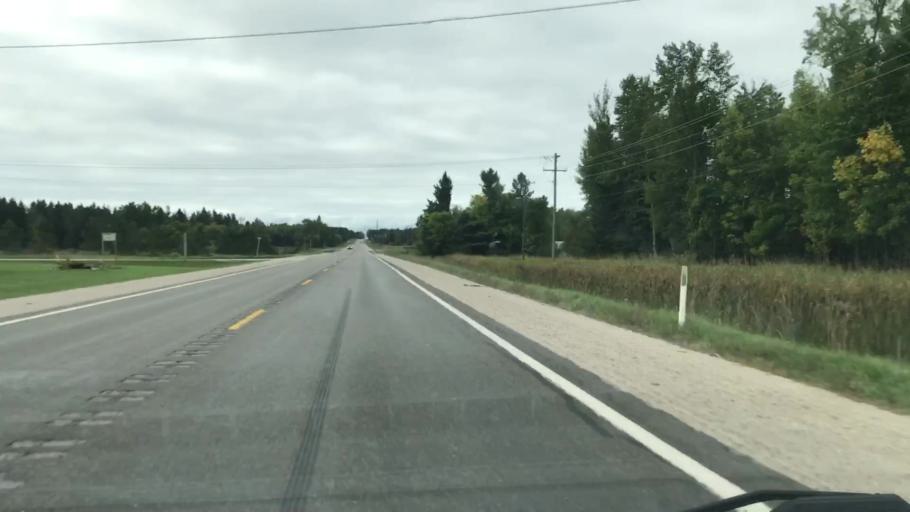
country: US
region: Michigan
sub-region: Luce County
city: Newberry
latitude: 46.1377
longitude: -85.5713
